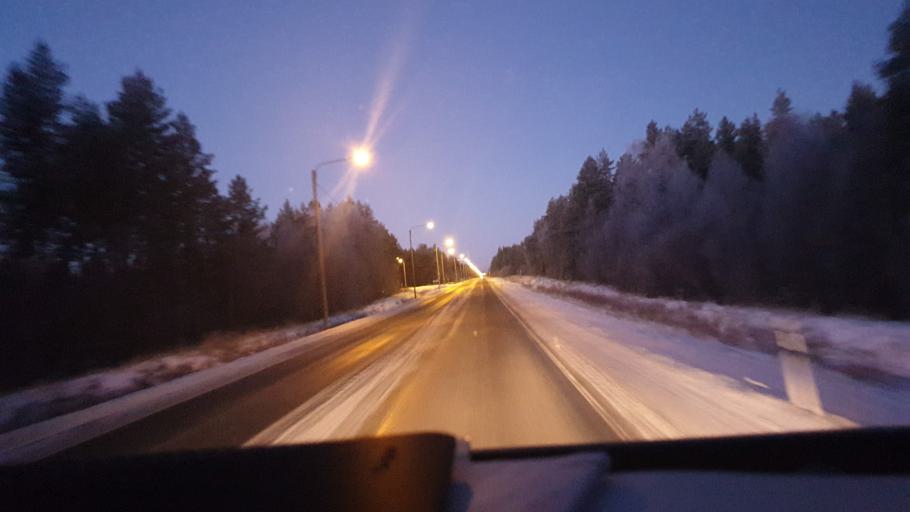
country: FI
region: Northern Ostrobothnia
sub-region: Raahe
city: Siikajoki
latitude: 64.6918
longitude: 24.6497
